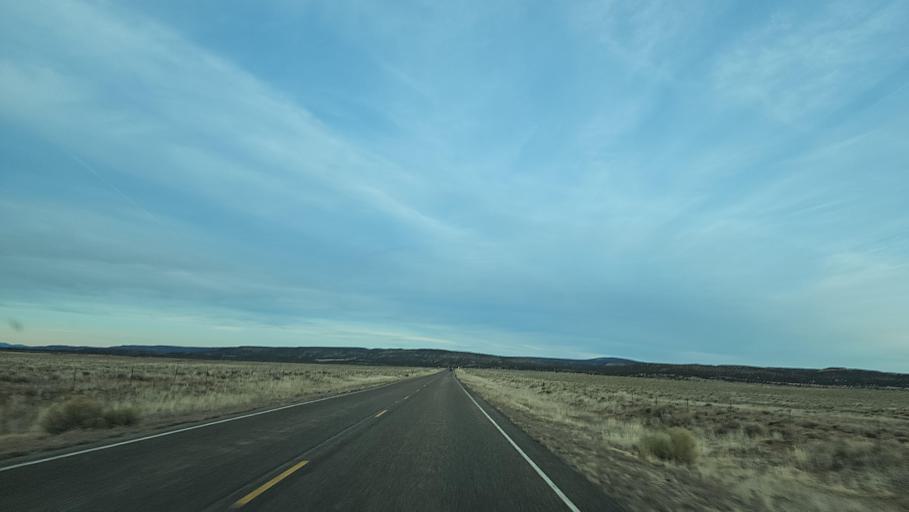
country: US
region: New Mexico
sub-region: Cibola County
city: Grants
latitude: 34.7061
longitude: -108.0172
